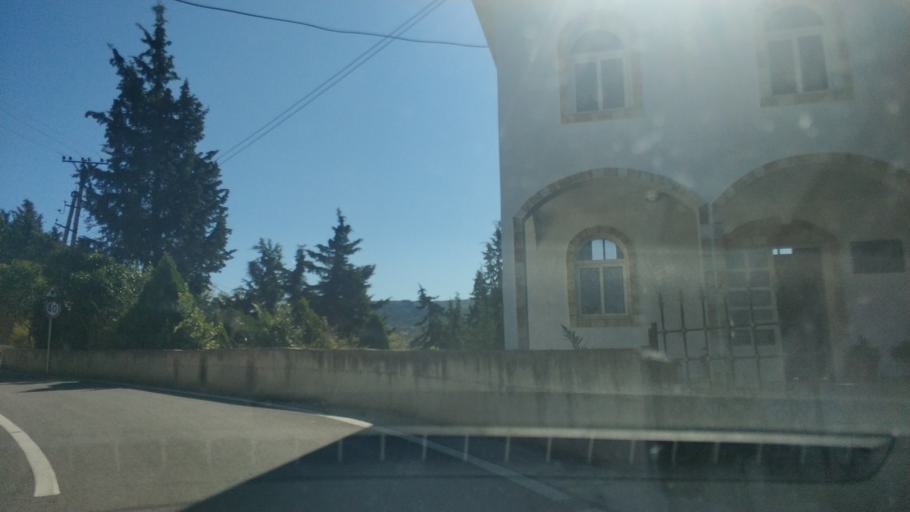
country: AL
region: Vlore
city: Vlore
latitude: 40.4432
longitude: 19.5192
